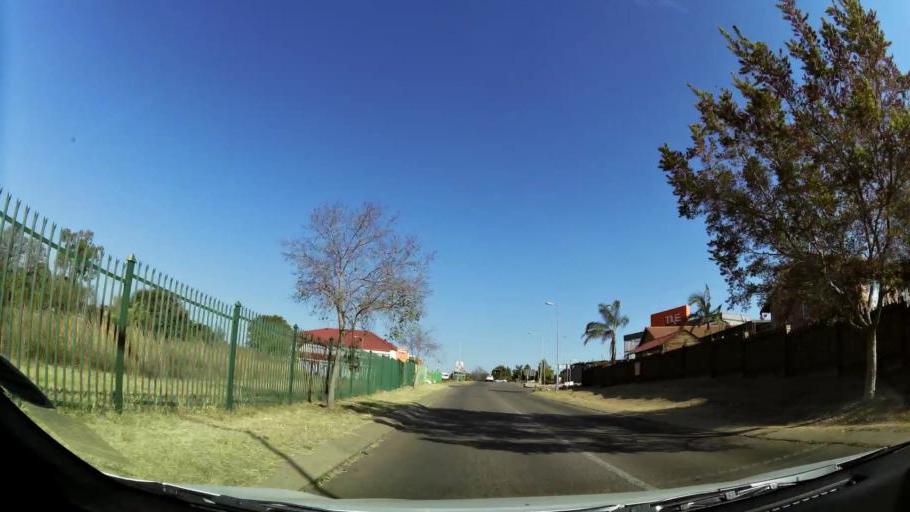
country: ZA
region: Gauteng
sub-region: City of Tshwane Metropolitan Municipality
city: Pretoria
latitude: -25.8026
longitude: 28.3025
